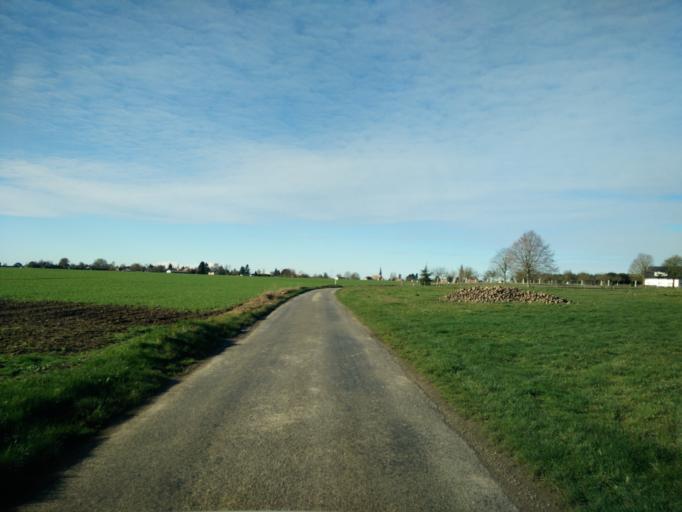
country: FR
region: Haute-Normandie
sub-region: Departement de l'Eure
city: Saint-Pierre-des-Fleurs
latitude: 49.1771
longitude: 0.9893
